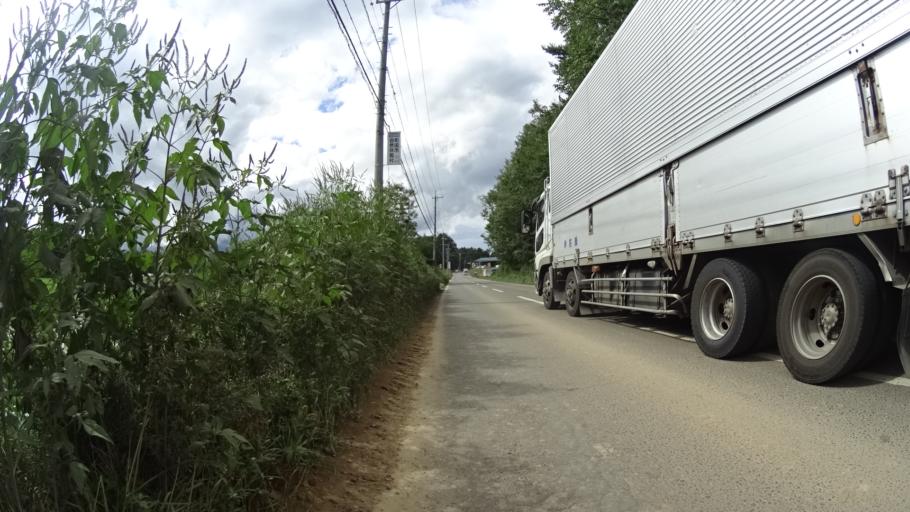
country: JP
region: Nagano
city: Saku
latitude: 35.9652
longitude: 138.5270
